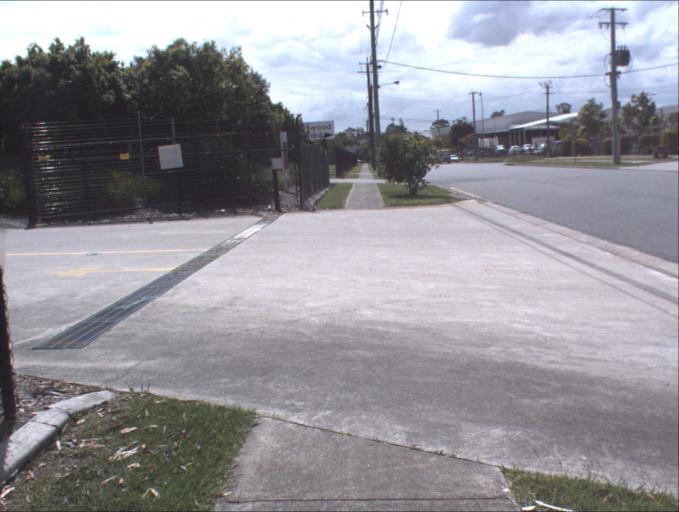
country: AU
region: Queensland
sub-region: Logan
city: Logan Reserve
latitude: -27.6844
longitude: 153.0757
